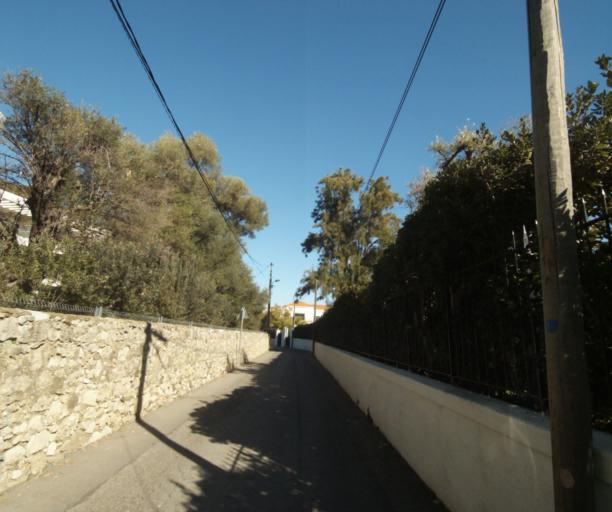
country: FR
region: Provence-Alpes-Cote d'Azur
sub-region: Departement des Alpes-Maritimes
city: Antibes
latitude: 43.5647
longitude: 7.1199
